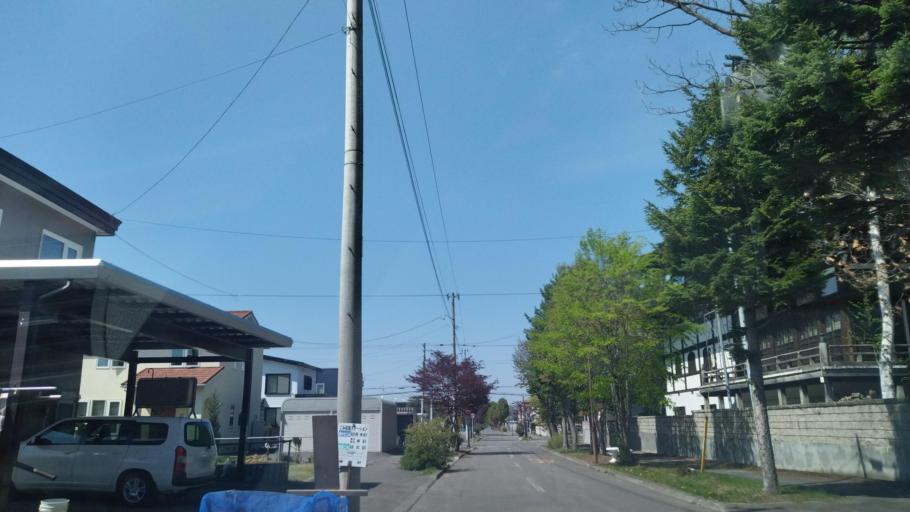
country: JP
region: Hokkaido
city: Obihiro
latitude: 42.9120
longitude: 143.0451
